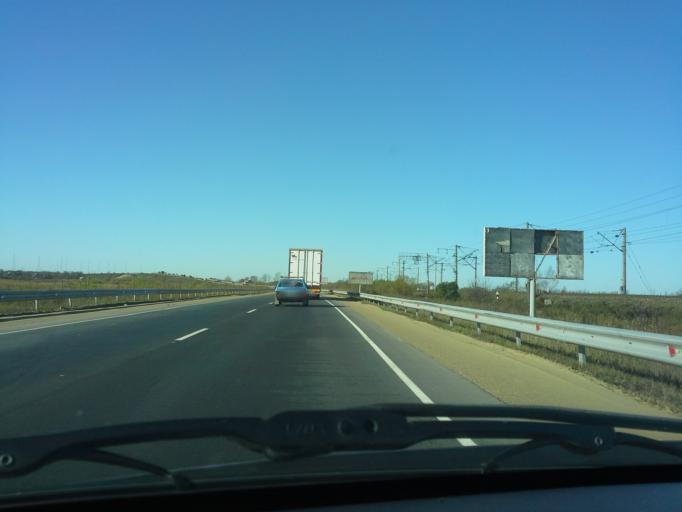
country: RU
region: Jewish Autonomous Oblast
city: Priamurskiy
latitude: 48.5255
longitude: 134.9284
